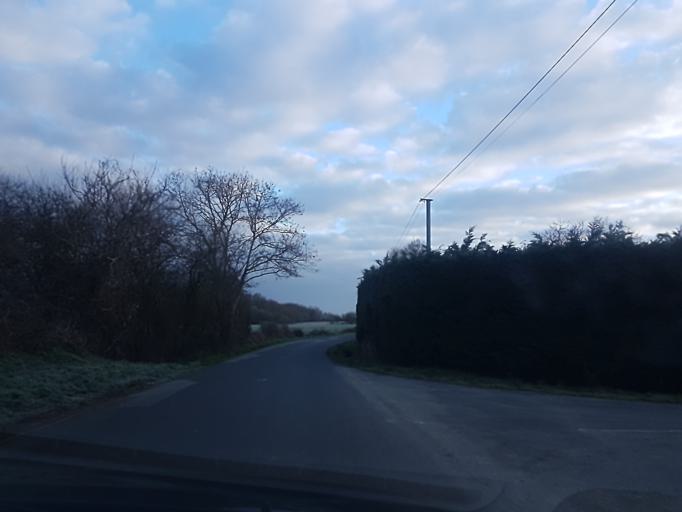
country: FR
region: Pays de la Loire
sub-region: Departement de la Loire-Atlantique
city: Saint-Mars-du-Desert
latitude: 47.3879
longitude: -1.4243
